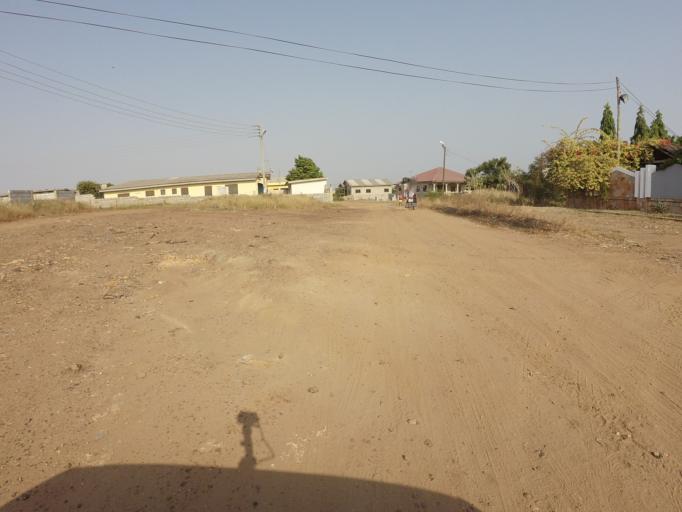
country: GH
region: Greater Accra
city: Tema
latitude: 5.7022
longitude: 0.0624
